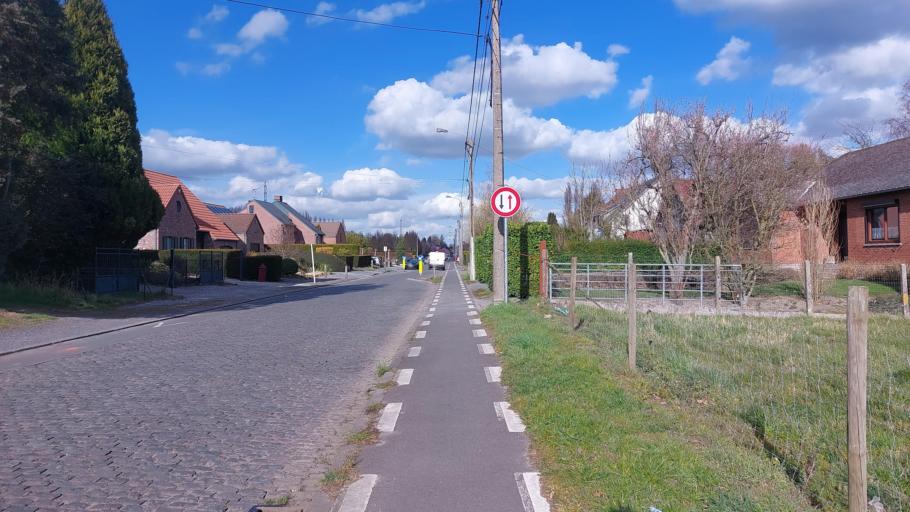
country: BE
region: Wallonia
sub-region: Province du Hainaut
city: Chasse Royale
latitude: 50.4299
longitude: 3.9516
